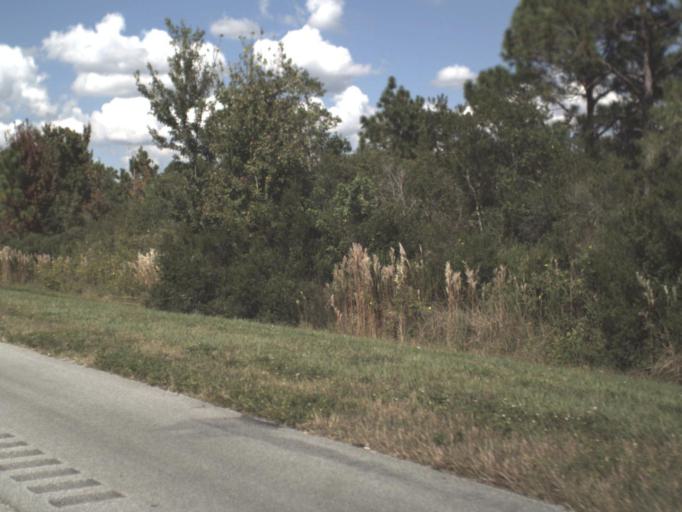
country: US
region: Florida
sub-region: Indian River County
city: Fellsmere
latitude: 27.7336
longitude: -80.9192
